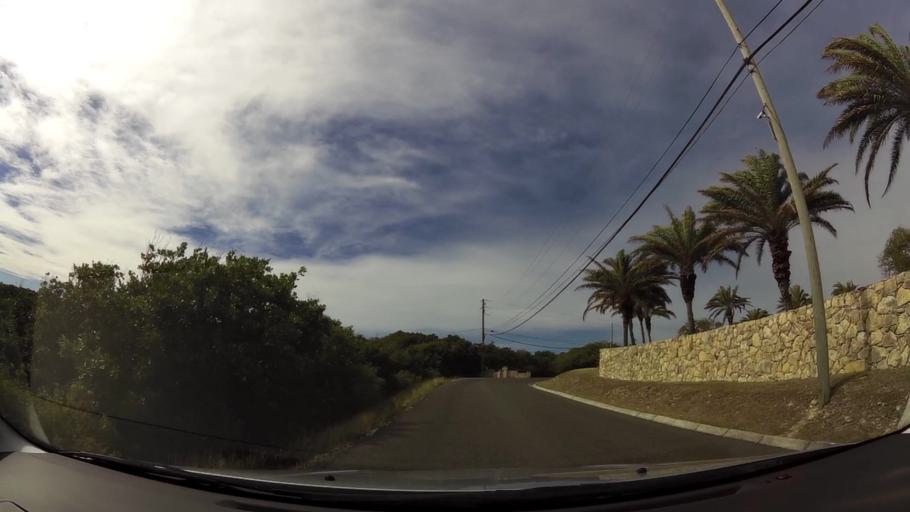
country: AG
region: Saint Paul
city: Falmouth
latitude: 17.0396
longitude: -61.6948
